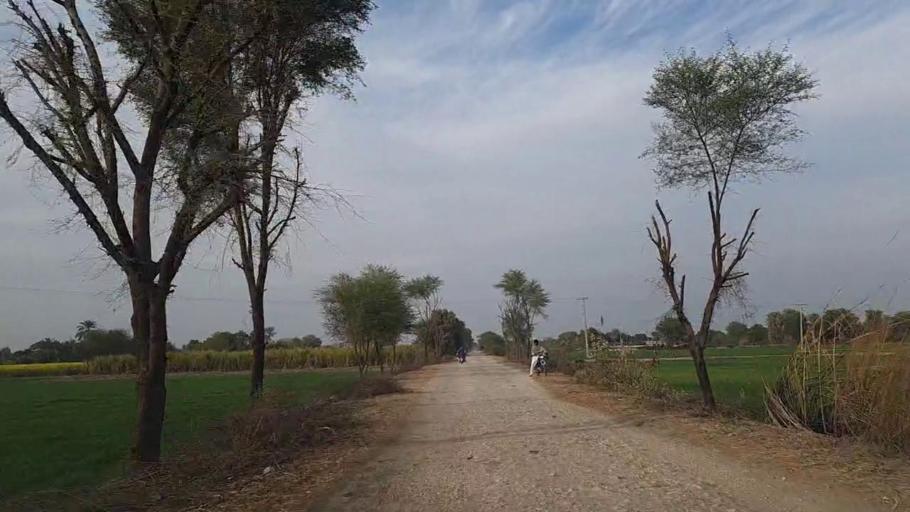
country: PK
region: Sindh
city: Daur
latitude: 26.5201
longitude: 68.4072
